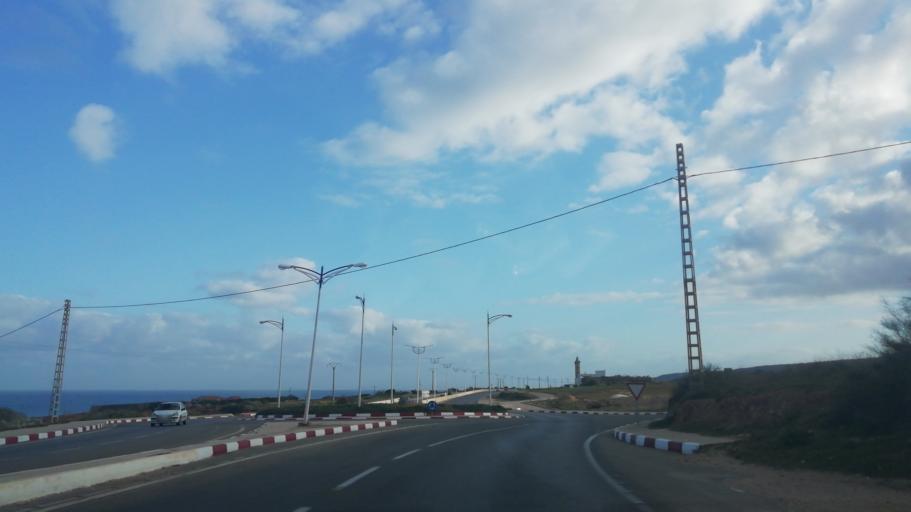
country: DZ
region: Mostaganem
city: Mostaganem
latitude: 36.0648
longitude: 0.1695
